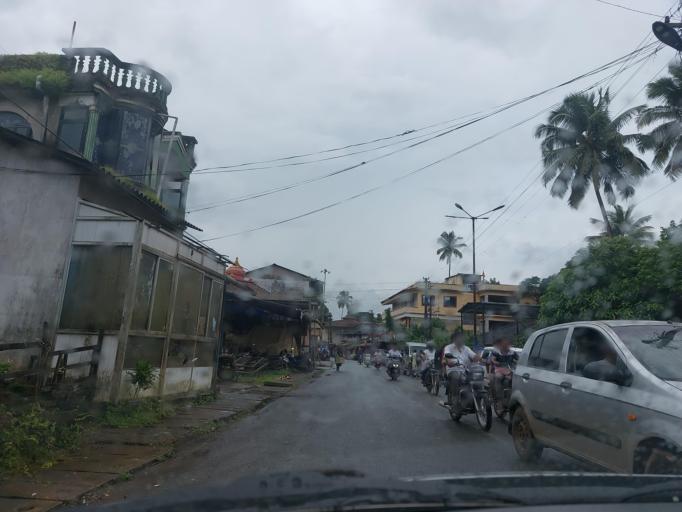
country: IN
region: Goa
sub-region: North Goa
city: Valpoy
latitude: 15.5322
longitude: 74.1371
